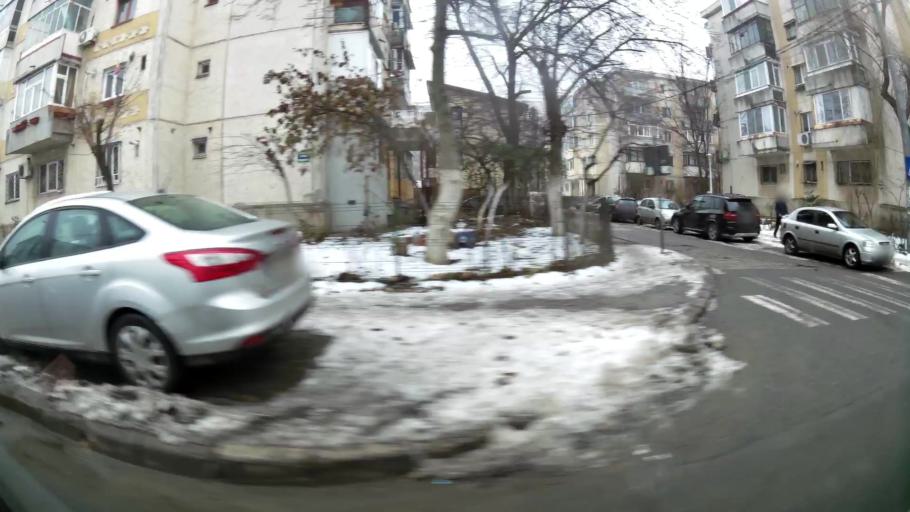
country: RO
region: Ilfov
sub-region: Comuna Chiajna
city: Rosu
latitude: 44.4400
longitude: 26.0118
